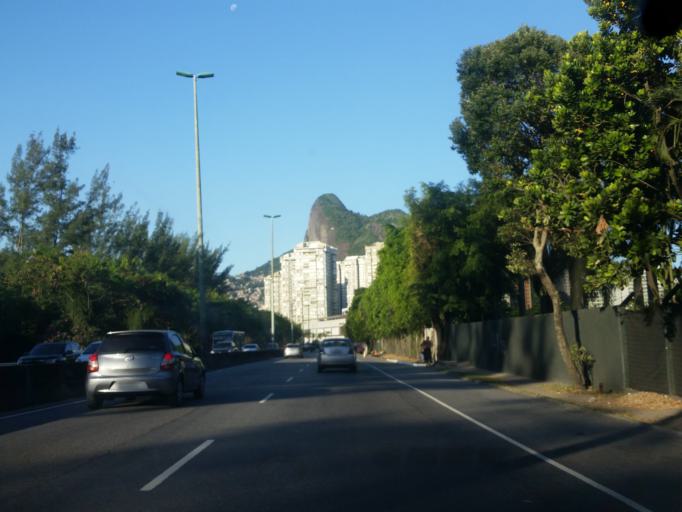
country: BR
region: Rio de Janeiro
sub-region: Rio De Janeiro
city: Rio de Janeiro
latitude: -22.9977
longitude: -43.2643
